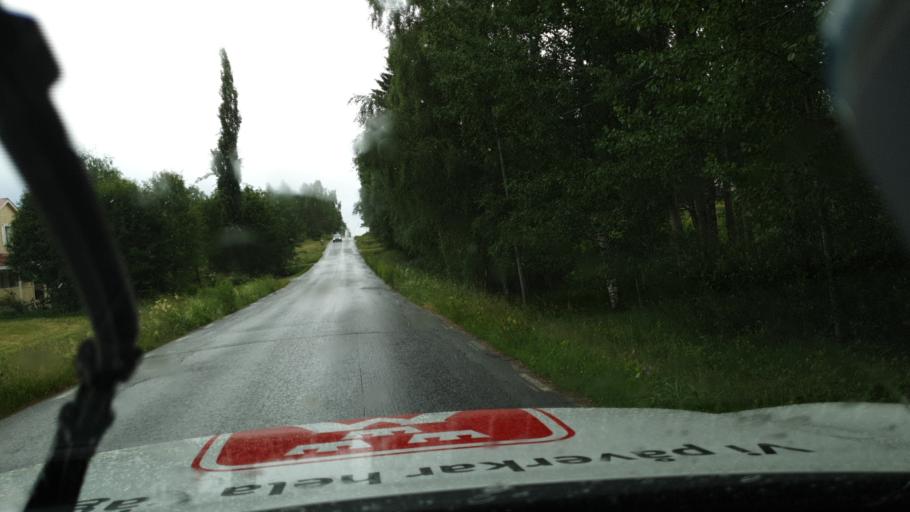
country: SE
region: Vaesterbotten
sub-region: Dorotea Kommun
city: Dorotea
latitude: 63.8216
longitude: 16.3998
